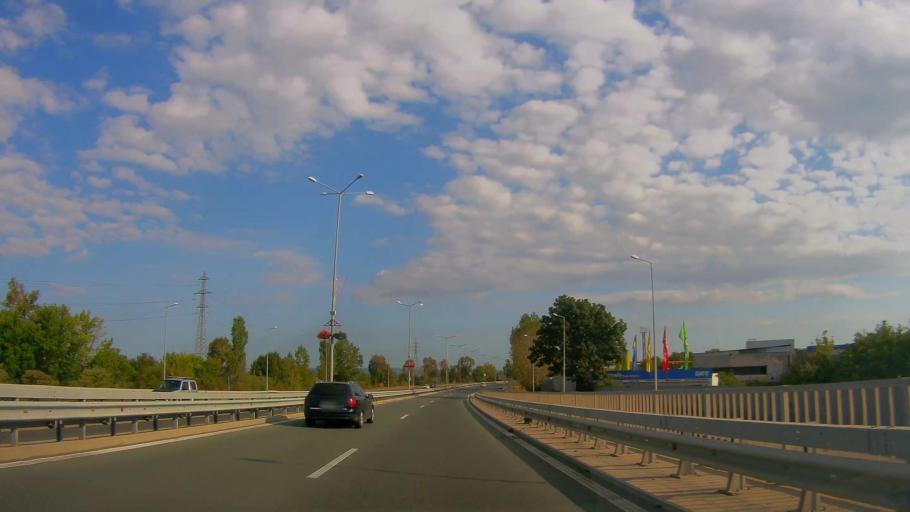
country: BG
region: Burgas
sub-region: Obshtina Burgas
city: Burgas
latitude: 42.4751
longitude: 27.4359
